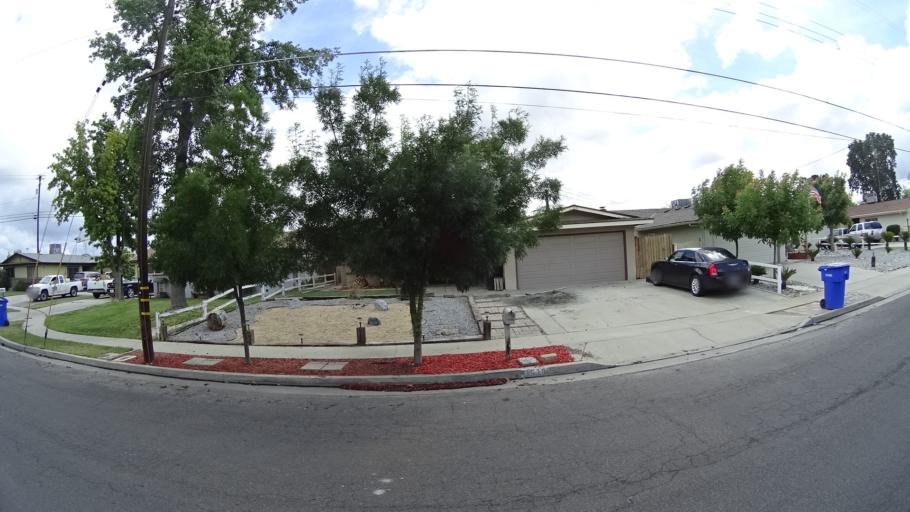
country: US
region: California
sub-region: Kings County
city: Hanford
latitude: 36.3418
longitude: -119.6621
